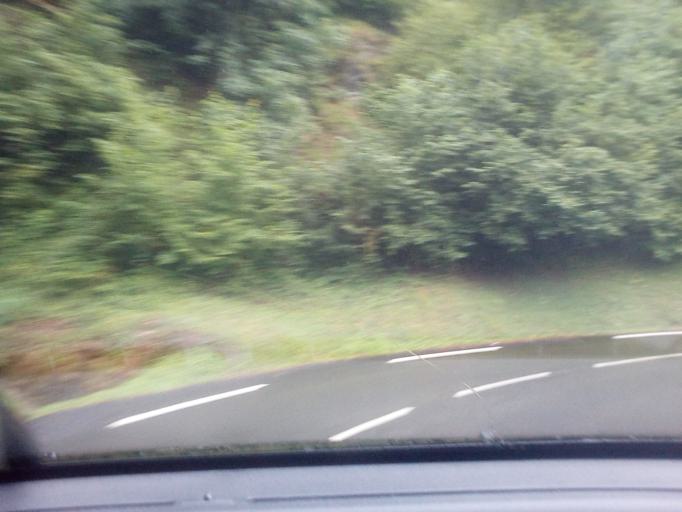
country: FR
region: Midi-Pyrenees
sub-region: Departement des Hautes-Pyrenees
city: Campan
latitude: 42.9364
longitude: 0.2086
